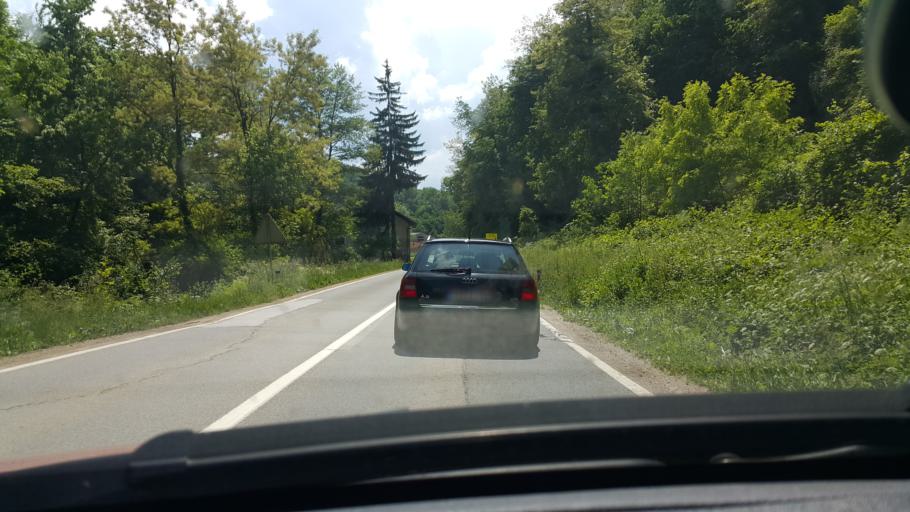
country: SI
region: Novo Mesto
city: Novo Mesto
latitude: 45.7801
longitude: 15.1782
